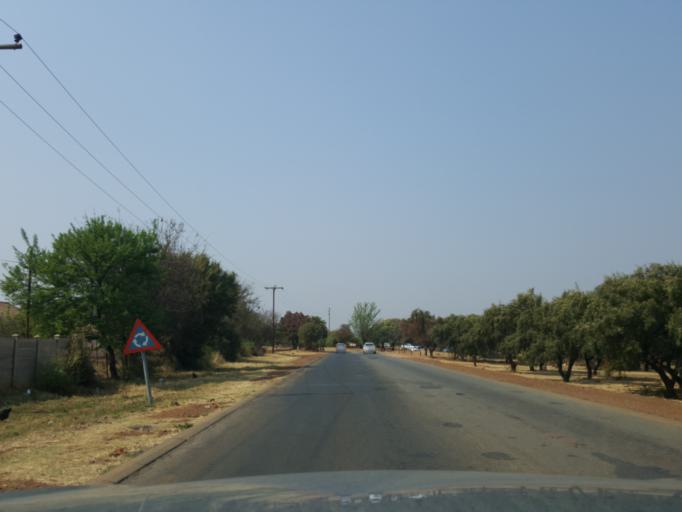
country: ZA
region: North-West
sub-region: Ngaka Modiri Molema District Municipality
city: Zeerust
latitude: -25.4976
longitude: 25.9841
